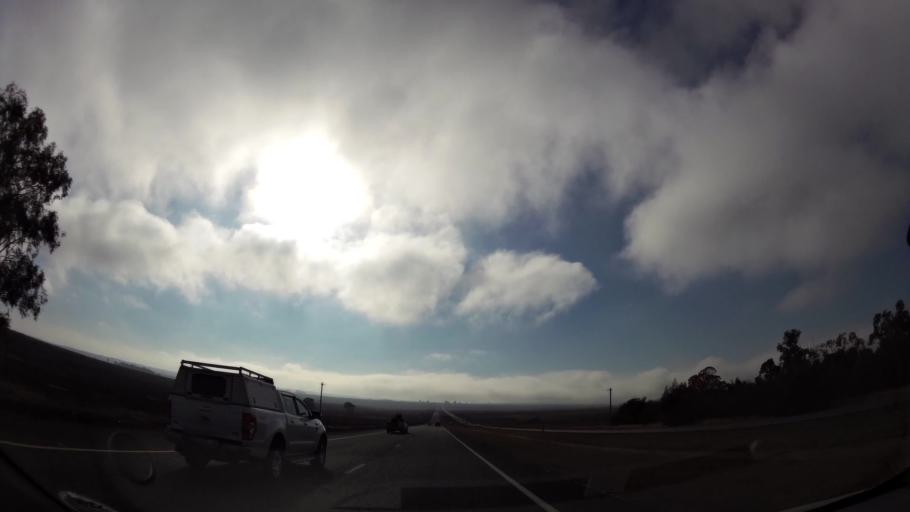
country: ZA
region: Mpumalanga
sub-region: Nkangala District Municipality
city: Delmas
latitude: -26.0348
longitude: 28.8571
